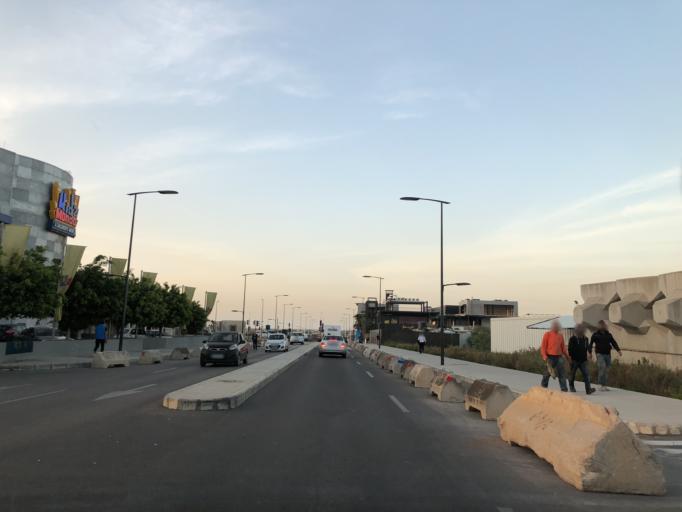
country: LB
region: Beyrouth
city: Beirut
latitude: 33.9044
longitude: 35.5059
